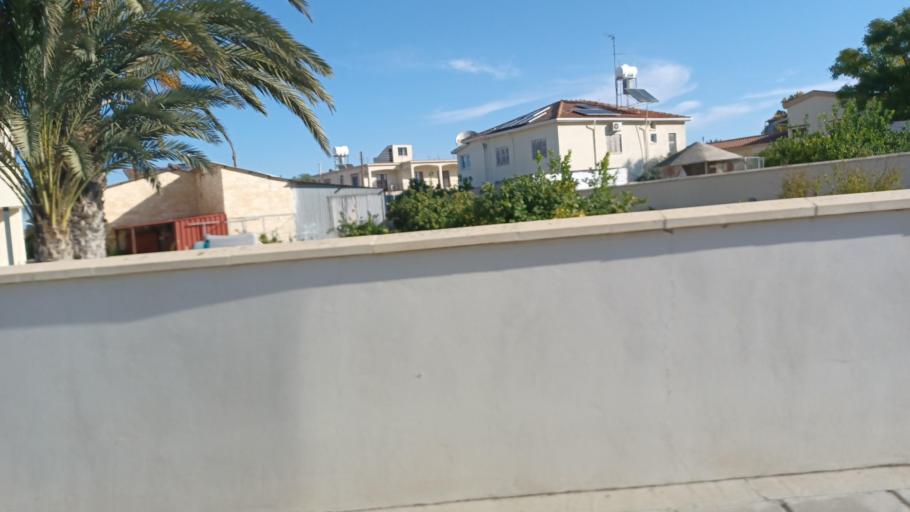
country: CY
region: Larnaka
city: Athienou
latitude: 35.0642
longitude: 33.5322
